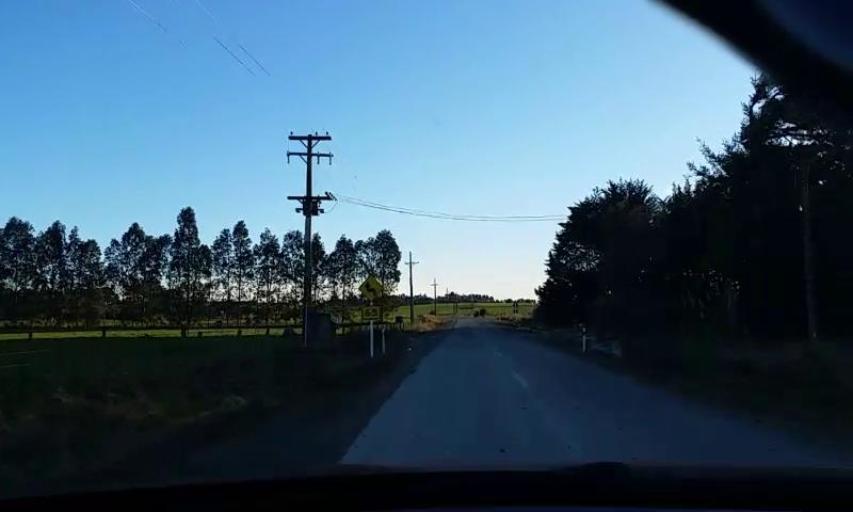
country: NZ
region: Southland
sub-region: Invercargill City
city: Invercargill
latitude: -46.2916
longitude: 168.4142
